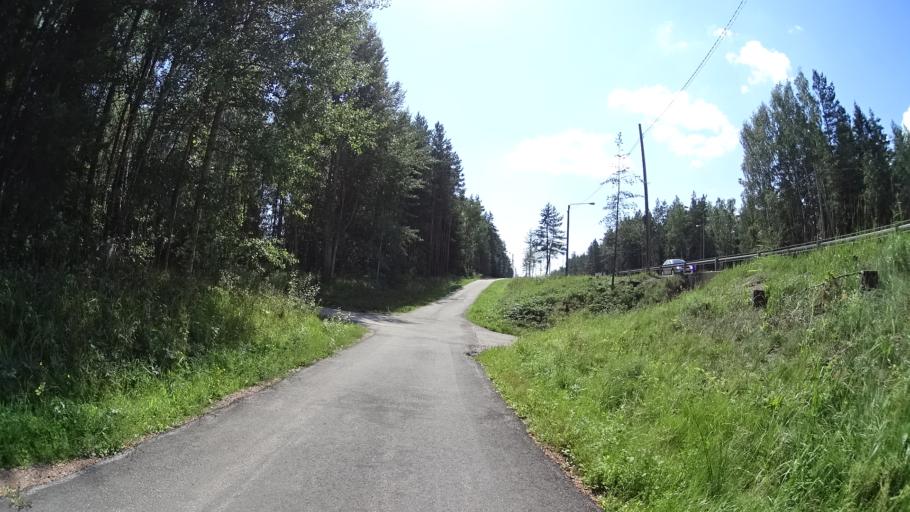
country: FI
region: Uusimaa
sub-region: Helsinki
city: Vantaa
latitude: 60.3193
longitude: 25.0007
